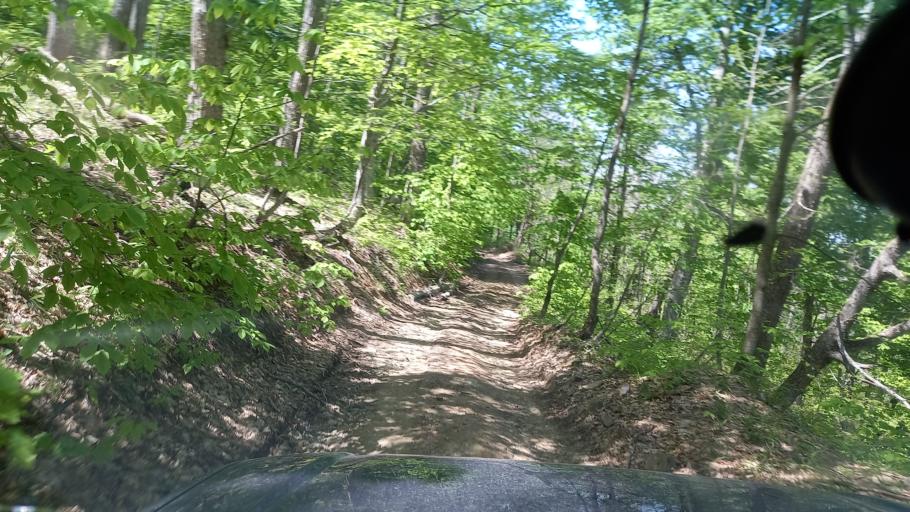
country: RU
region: Krasnodarskiy
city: Tuapse
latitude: 44.2492
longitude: 39.2974
